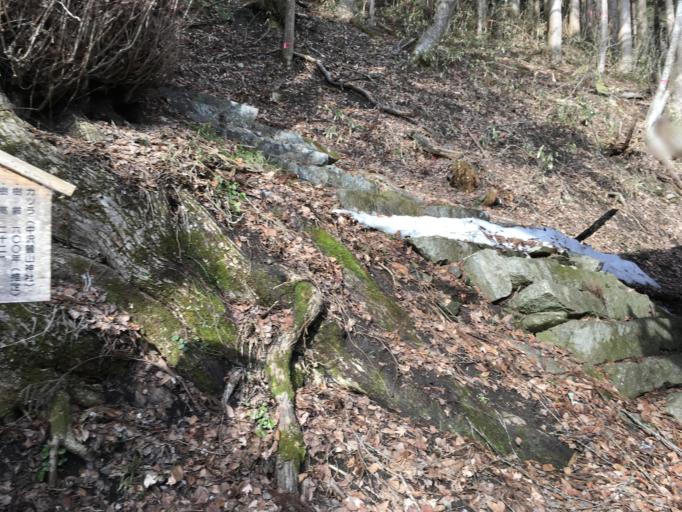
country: JP
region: Iwate
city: Tono
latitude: 39.2378
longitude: 141.3382
